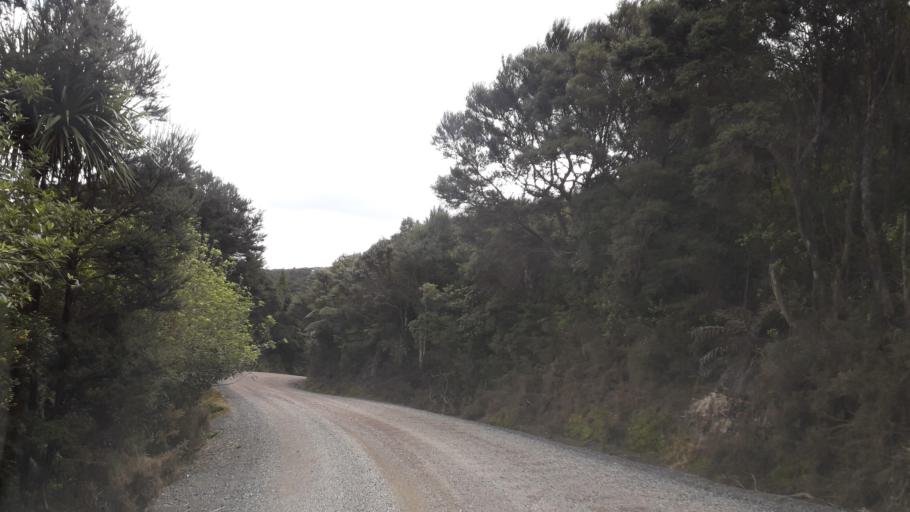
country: NZ
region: Northland
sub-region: Far North District
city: Paihia
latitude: -35.3159
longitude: 174.2258
